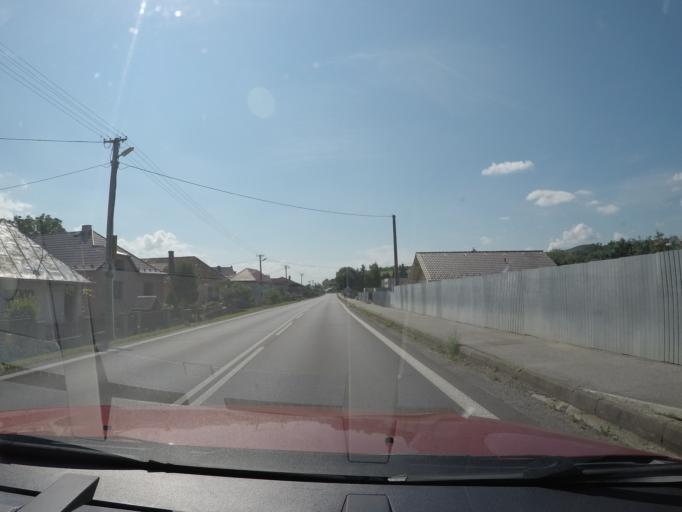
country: SK
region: Presovsky
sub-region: Okres Presov
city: Presov
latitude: 48.8762
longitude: 21.2465
